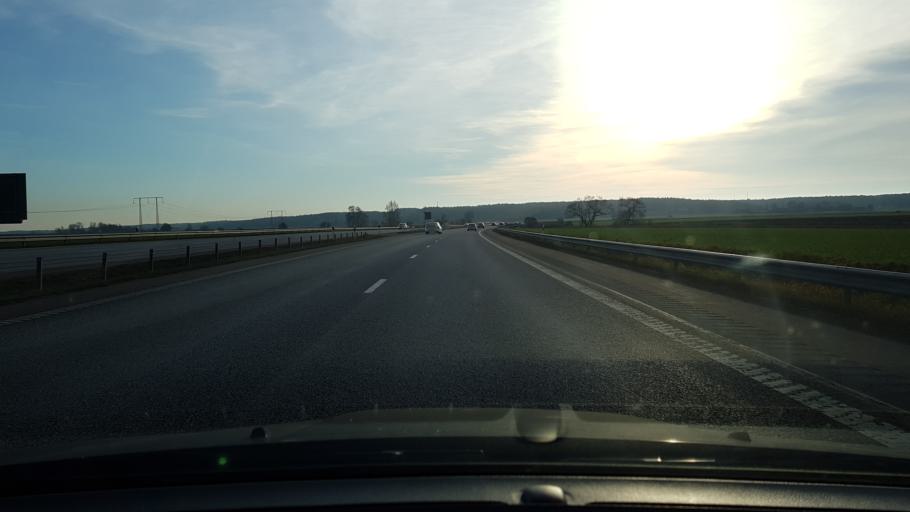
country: SE
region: Uppsala
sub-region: Uppsala Kommun
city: Saevja
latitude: 59.8185
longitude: 17.7531
